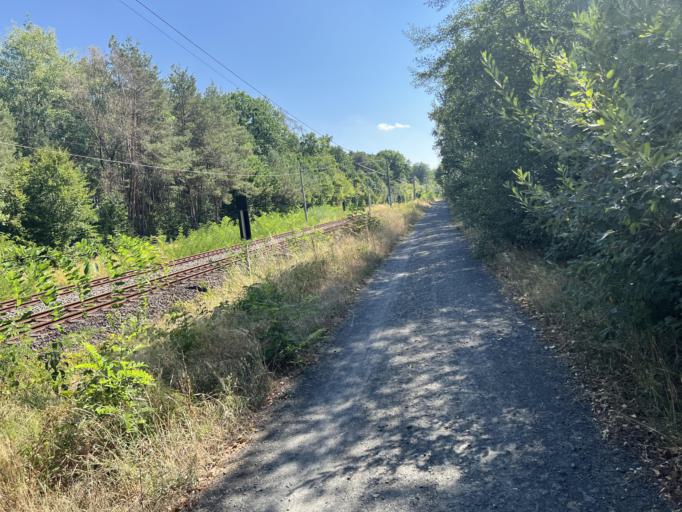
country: DE
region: Hesse
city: Obertshausen
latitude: 50.0811
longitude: 8.8318
